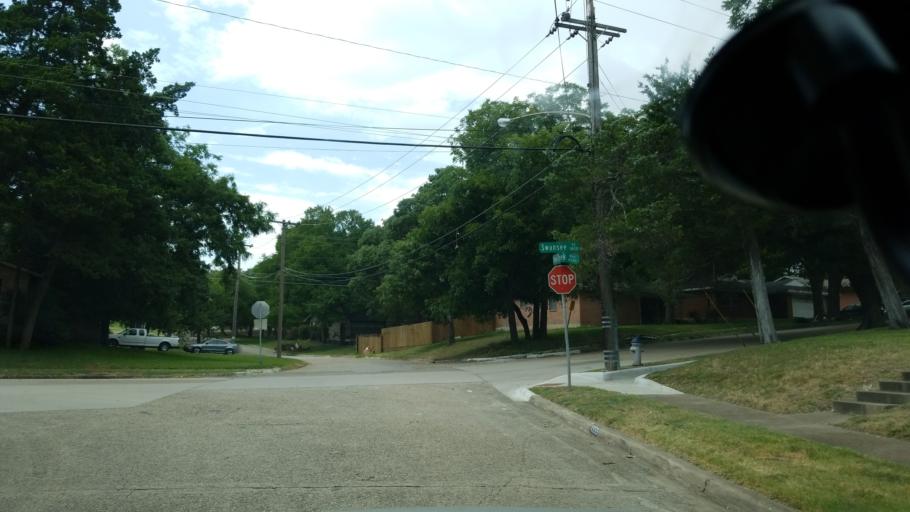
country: US
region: Texas
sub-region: Dallas County
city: Cockrell Hill
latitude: 32.6853
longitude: -96.8512
